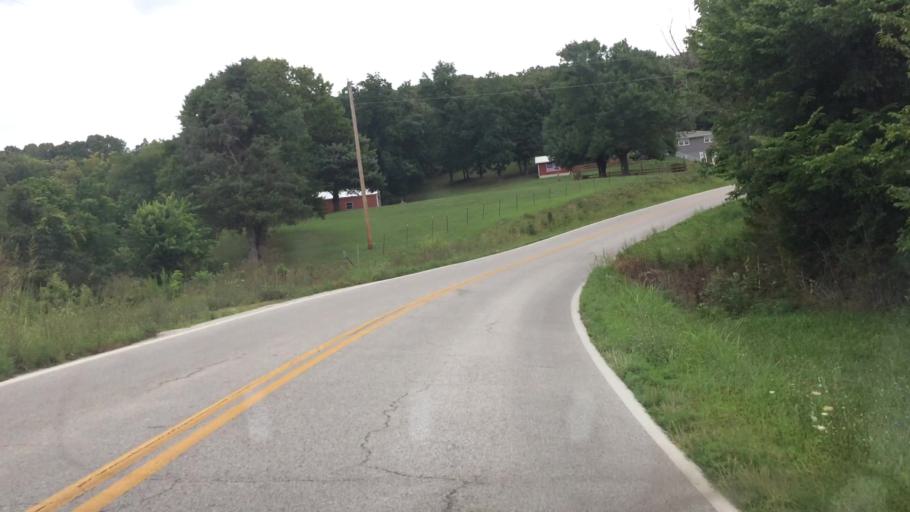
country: US
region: Missouri
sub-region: Greene County
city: Strafford
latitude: 37.2961
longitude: -93.0855
